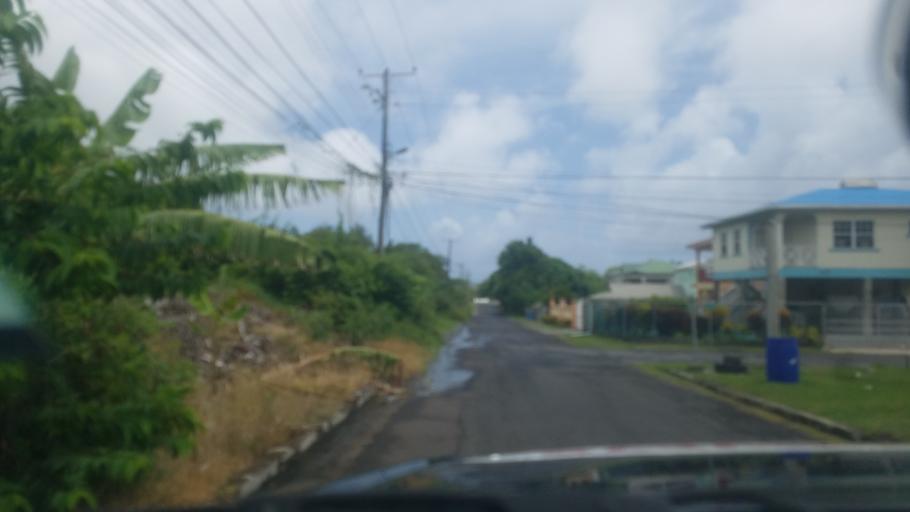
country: LC
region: Laborie Quarter
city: Laborie
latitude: 13.7459
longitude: -60.9718
